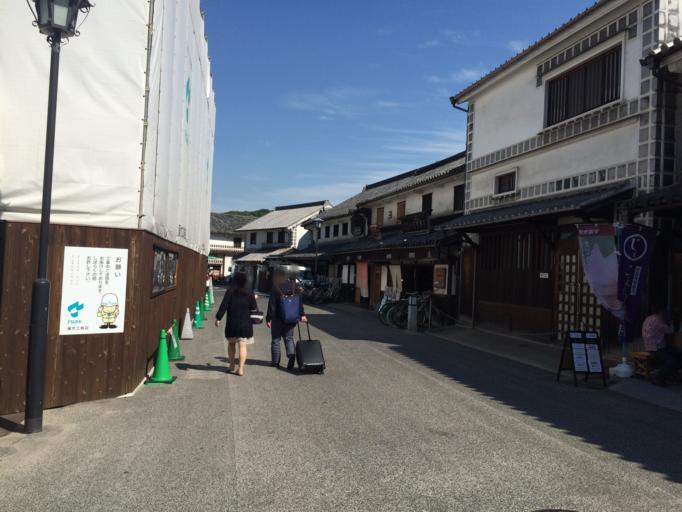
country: JP
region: Okayama
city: Kurashiki
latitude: 34.5966
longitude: 133.7722
